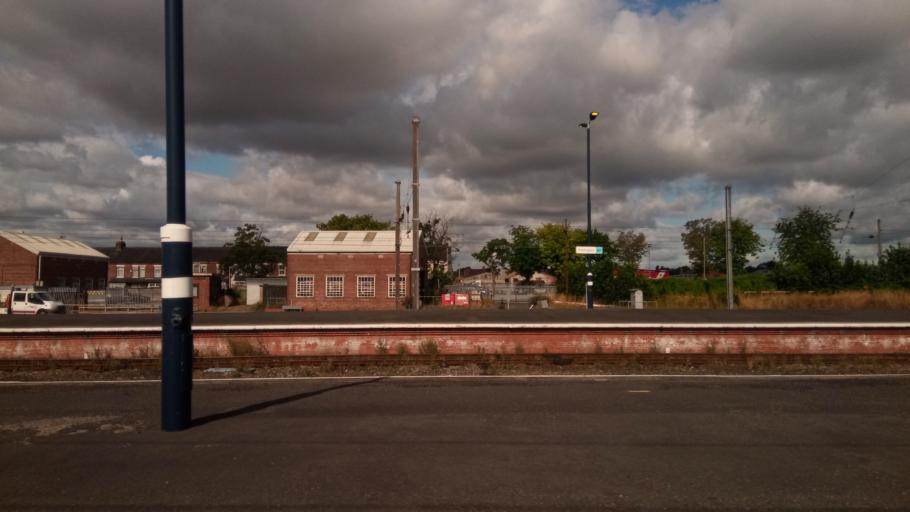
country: GB
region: England
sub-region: Darlington
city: Darlington
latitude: 54.5192
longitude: -1.5468
